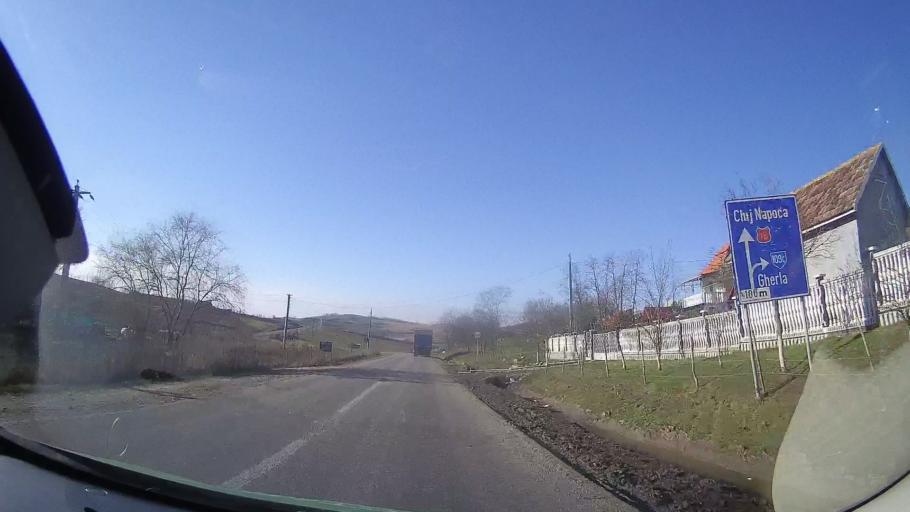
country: RO
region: Cluj
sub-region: Comuna Camarasu
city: Camarasu
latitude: 46.8031
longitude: 24.1529
